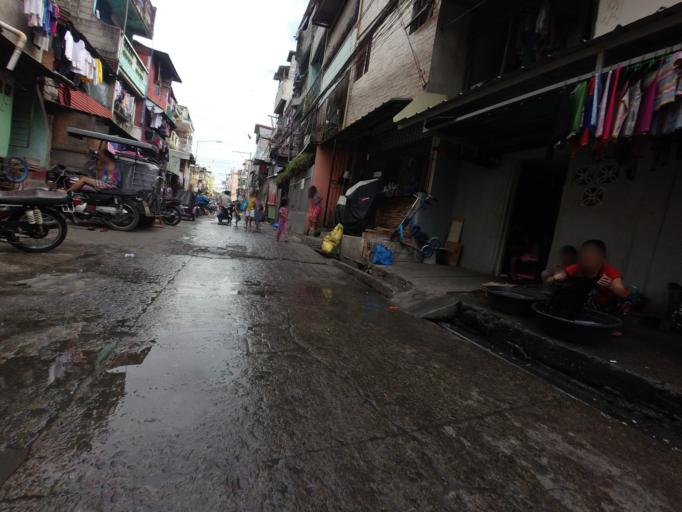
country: PH
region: Calabarzon
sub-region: Province of Rizal
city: Pateros
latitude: 14.5603
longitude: 121.0878
